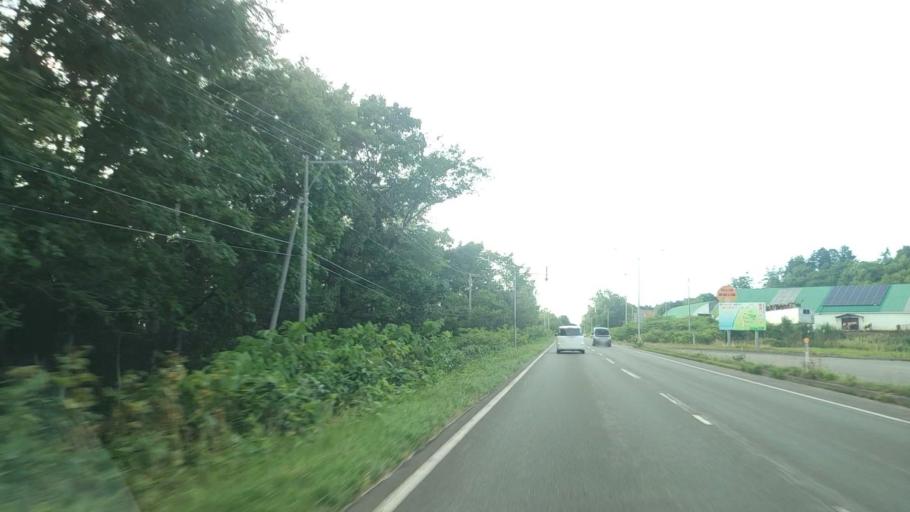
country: JP
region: Hokkaido
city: Makubetsu
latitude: 45.0437
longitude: 141.7547
